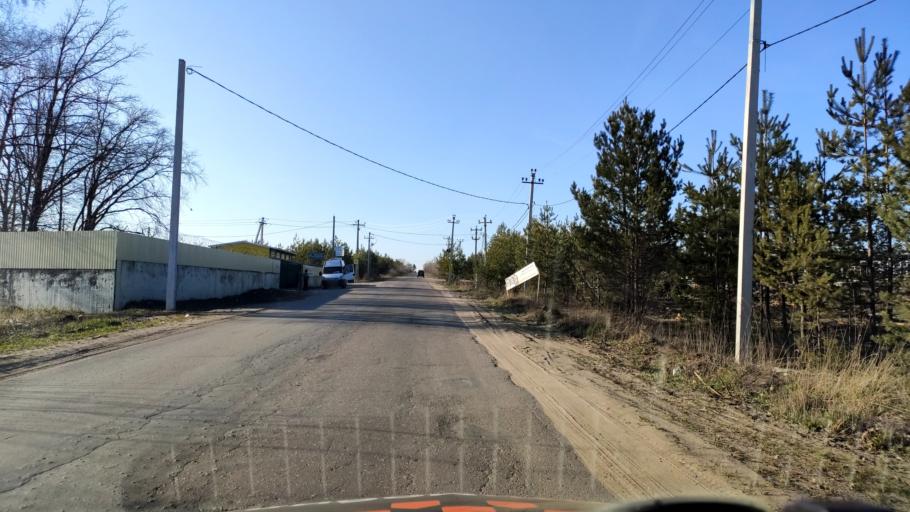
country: RU
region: Voronezj
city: Podgornoye
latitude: 51.8300
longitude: 39.2060
